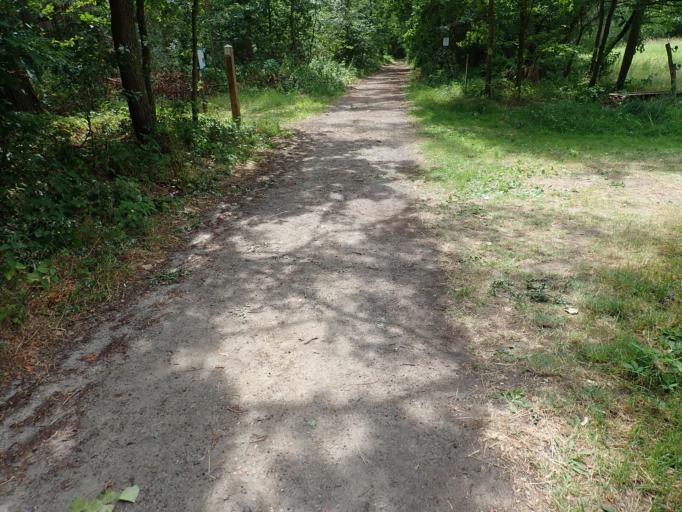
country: BE
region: Flanders
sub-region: Provincie Vlaams-Brabant
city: Keerbergen
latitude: 50.9984
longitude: 4.6198
